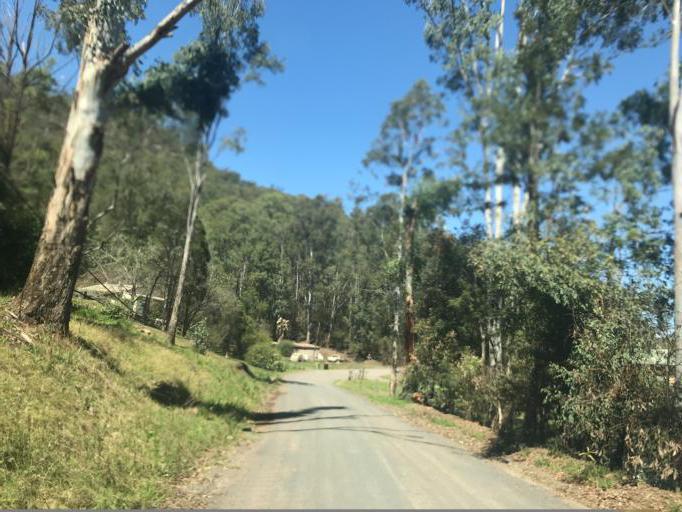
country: AU
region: New South Wales
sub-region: Hornsby Shire
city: Glenorie
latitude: -33.2599
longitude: 150.9723
